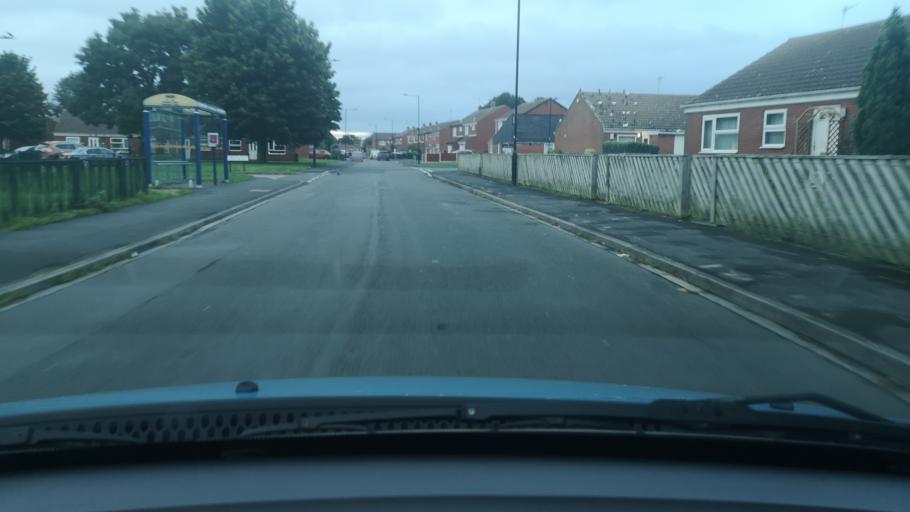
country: GB
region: England
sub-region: Doncaster
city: Askern
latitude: 53.6144
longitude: -1.1399
